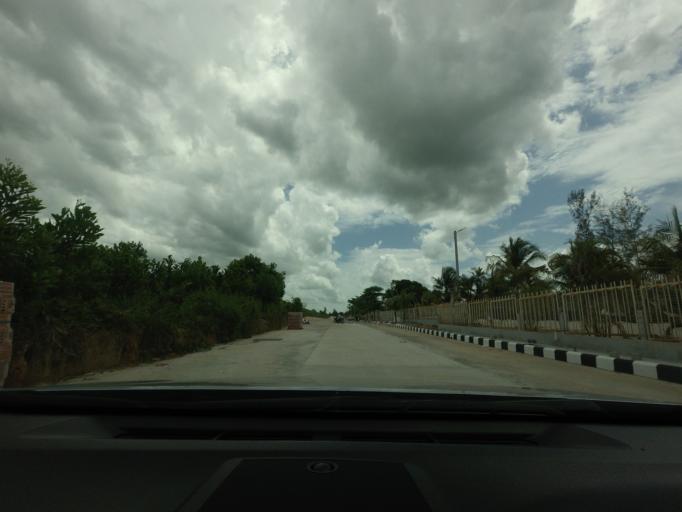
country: TH
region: Songkhla
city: Sadao
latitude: 6.5319
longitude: 100.4107
